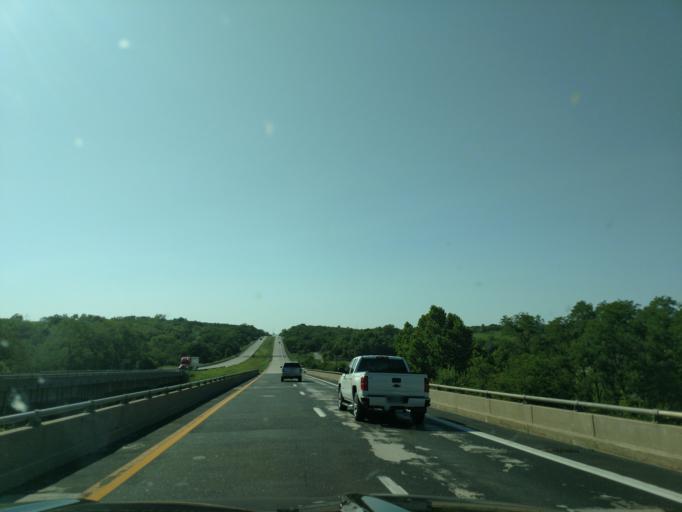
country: US
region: Missouri
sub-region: Andrew County
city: Savannah
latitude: 39.9013
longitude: -94.8807
